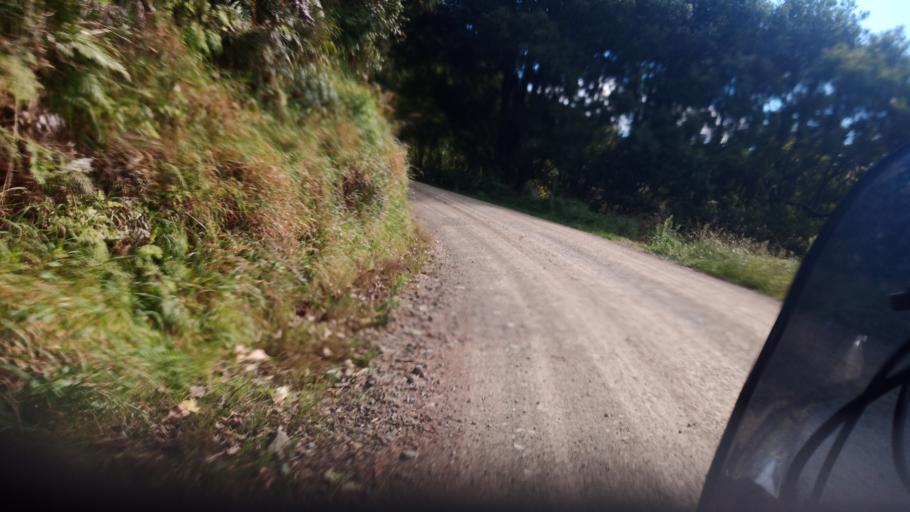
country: NZ
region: Bay of Plenty
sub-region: Opotiki District
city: Opotiki
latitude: -38.3440
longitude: 177.5834
